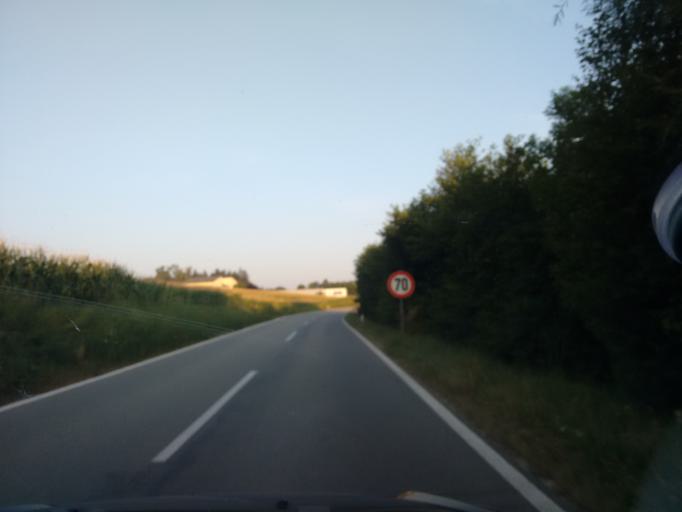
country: AT
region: Upper Austria
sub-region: Politischer Bezirk Grieskirchen
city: Bad Schallerbach
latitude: 48.1915
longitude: 13.9468
